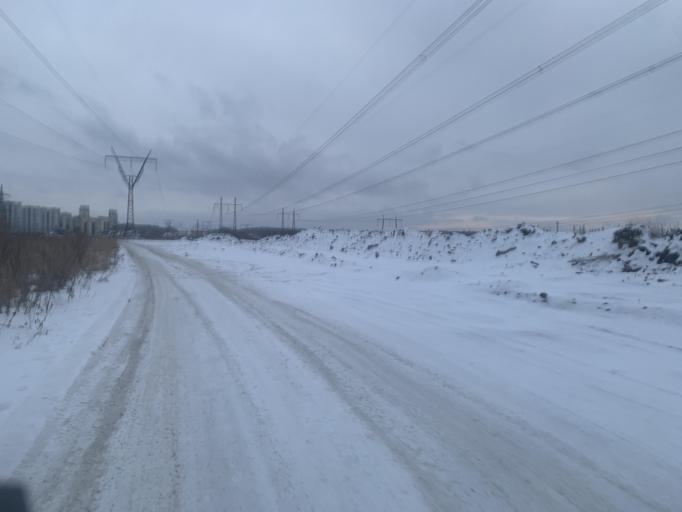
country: RU
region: Chelyabinsk
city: Roshchino
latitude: 55.1857
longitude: 61.2573
